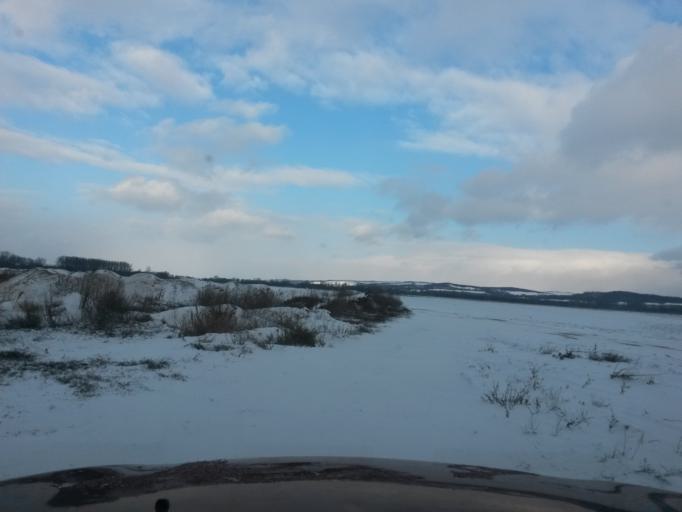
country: SK
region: Kosicky
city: Kosice
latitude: 48.6298
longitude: 21.3372
